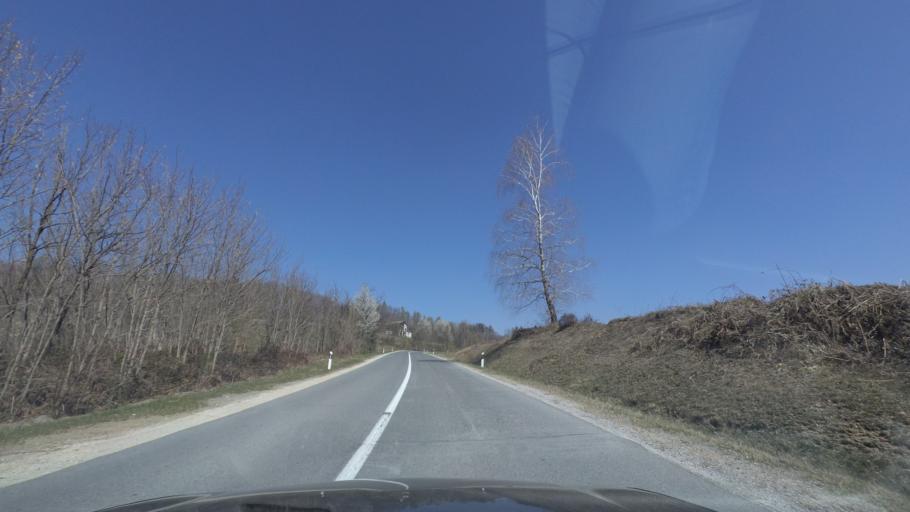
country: HR
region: Karlovacka
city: Vojnic
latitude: 45.3421
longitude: 15.7687
